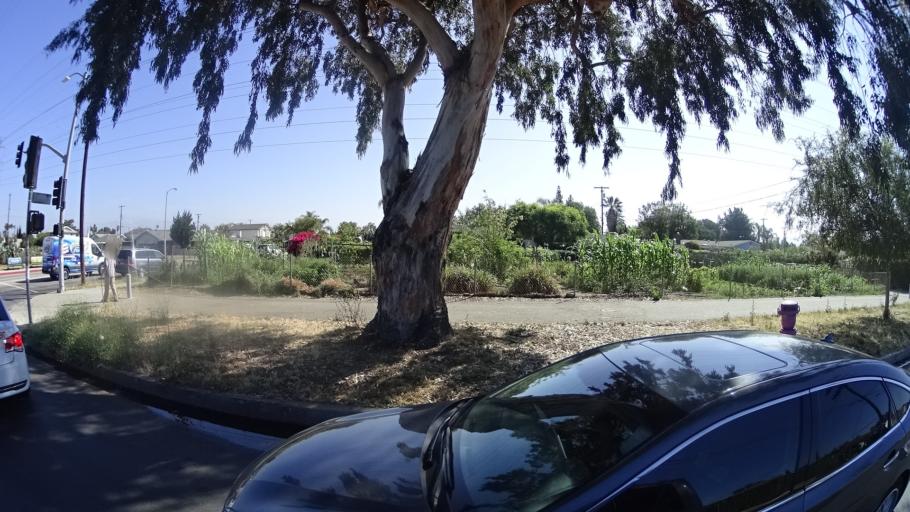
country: US
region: California
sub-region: Los Angeles County
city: Van Nuys
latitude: 34.2311
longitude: -118.4261
